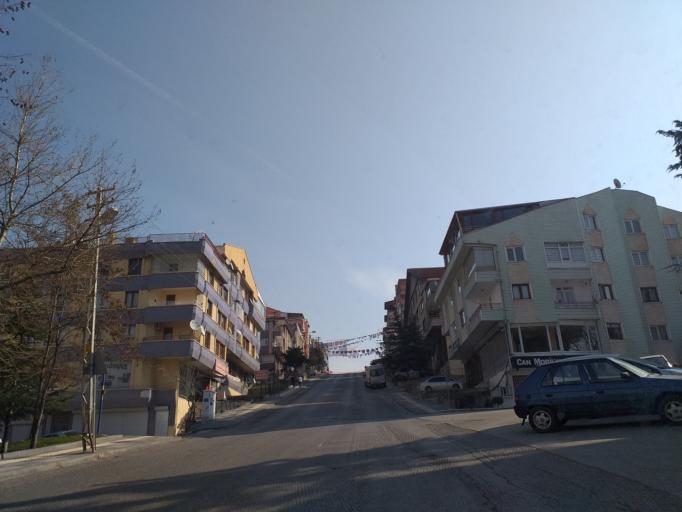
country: TR
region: Ankara
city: Ankara
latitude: 39.9835
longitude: 32.8416
